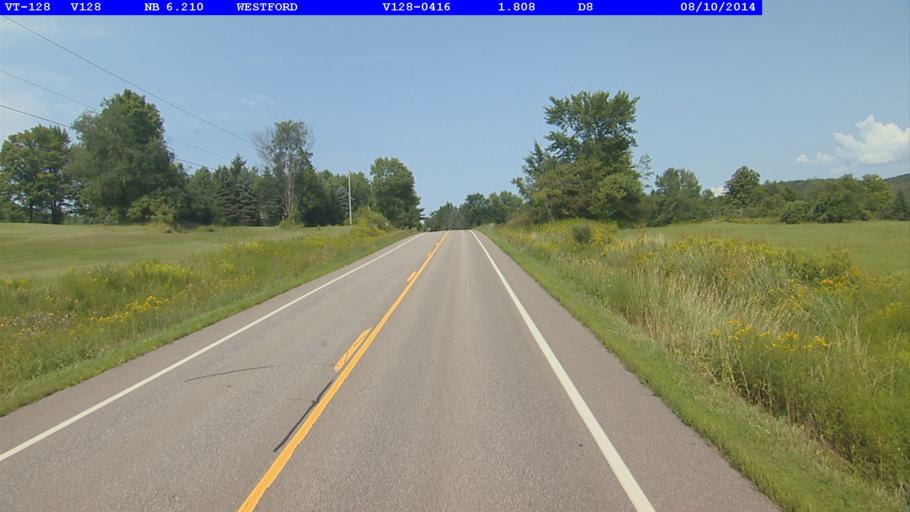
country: US
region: Vermont
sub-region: Chittenden County
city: Jericho
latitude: 44.5839
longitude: -73.0164
